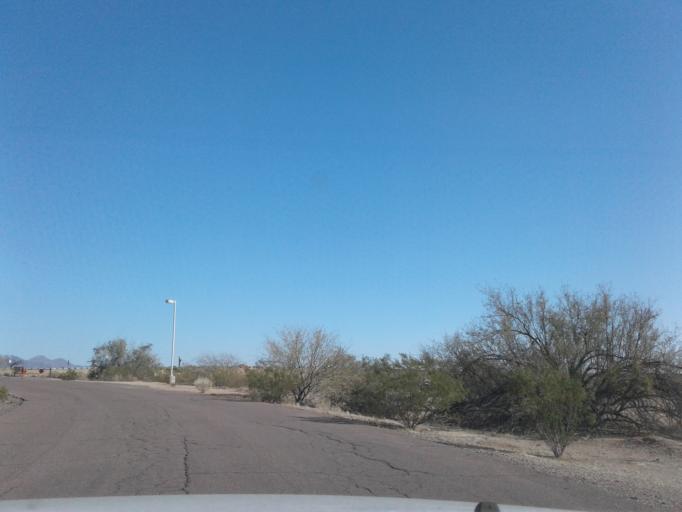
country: US
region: Arizona
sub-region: Maricopa County
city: Paradise Valley
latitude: 33.6615
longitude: -111.9803
